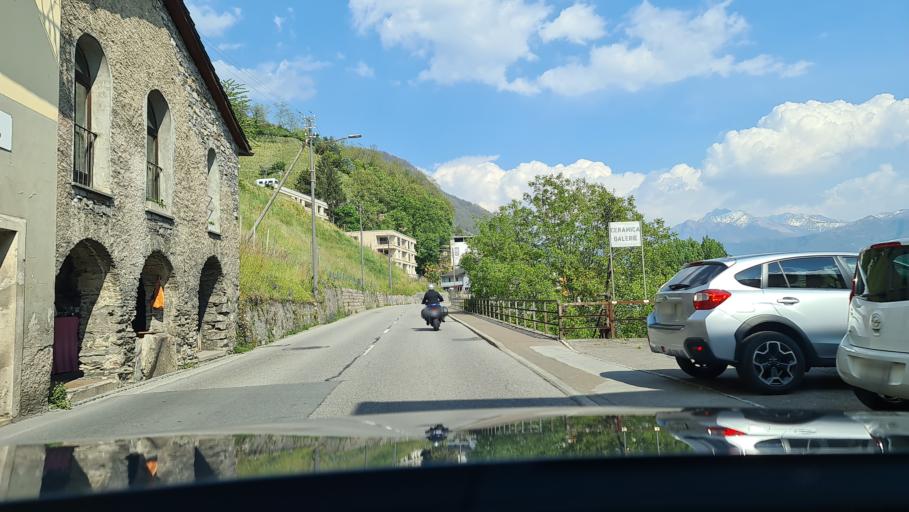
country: CH
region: Ticino
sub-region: Locarno District
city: Gordola
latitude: 46.1823
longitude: 8.8535
